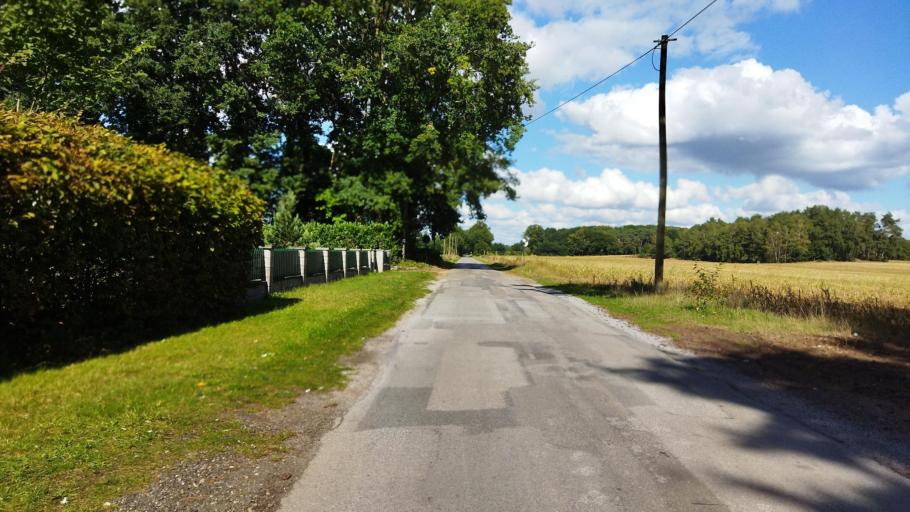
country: DE
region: Lower Saxony
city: Emsburen
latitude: 52.4347
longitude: 7.3398
